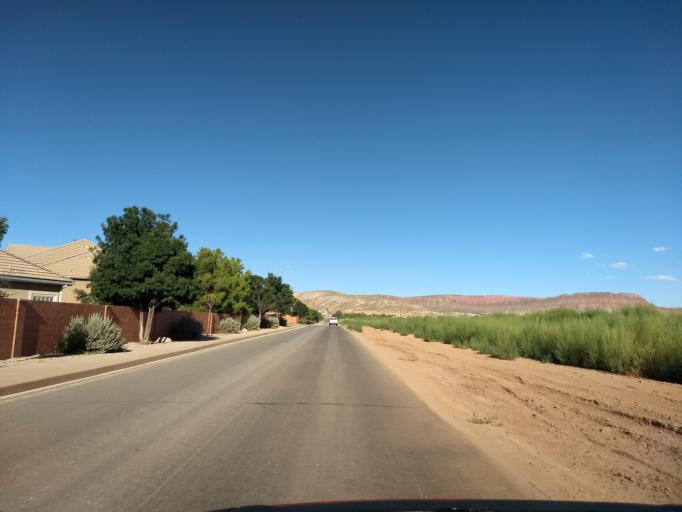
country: US
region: Utah
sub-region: Washington County
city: Washington
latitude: 37.0959
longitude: -113.5167
